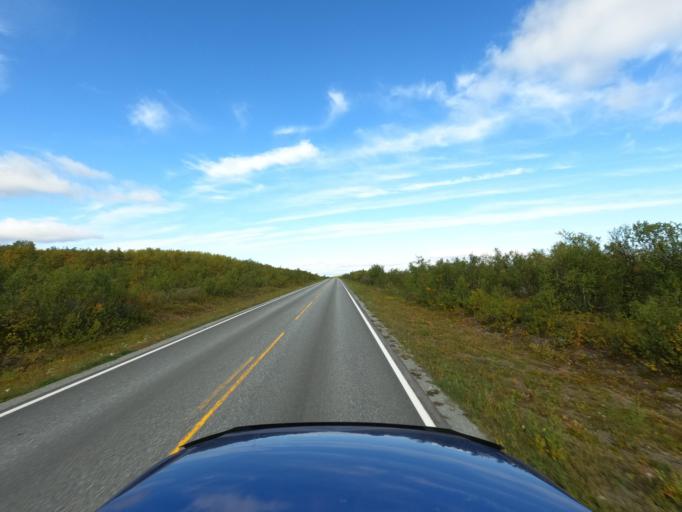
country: NO
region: Finnmark Fylke
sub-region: Karasjok
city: Karasjohka
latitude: 69.6837
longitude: 25.2620
